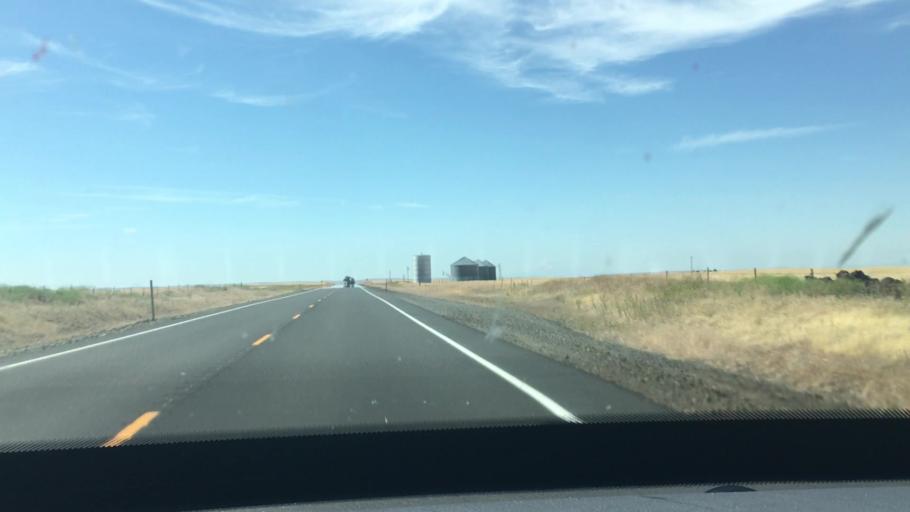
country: US
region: Oregon
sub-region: Sherman County
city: Moro
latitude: 45.2977
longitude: -120.7581
